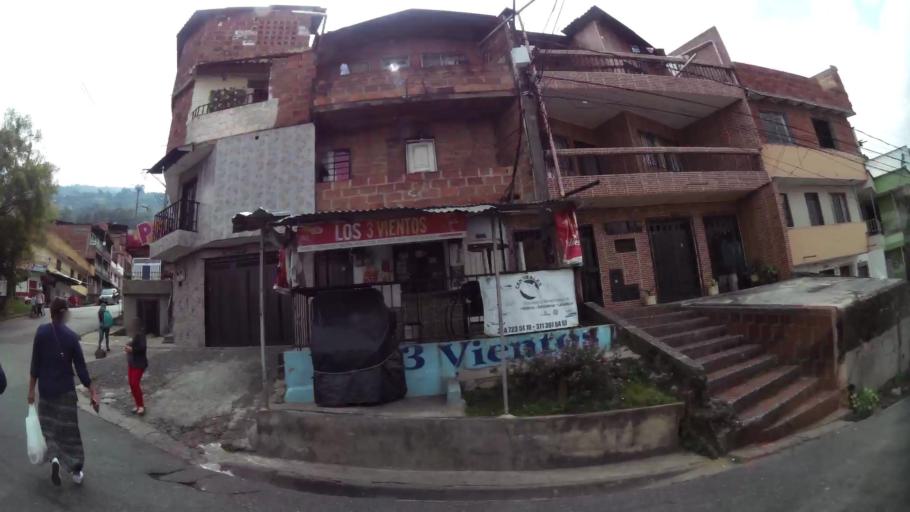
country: CO
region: Antioquia
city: Medellin
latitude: 6.2784
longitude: -75.5512
